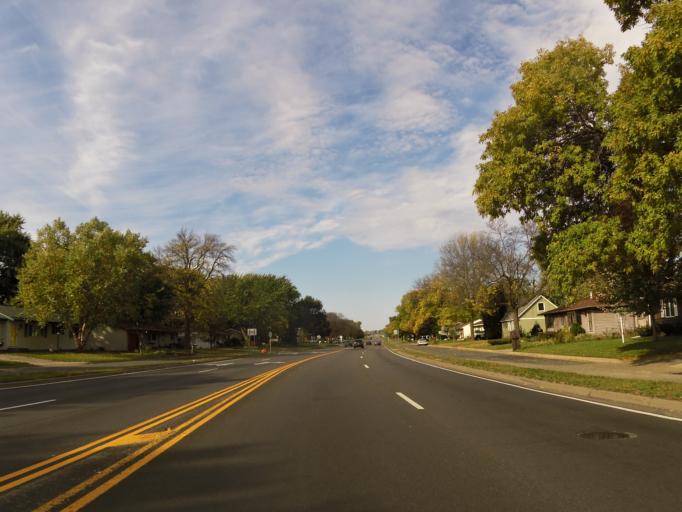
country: US
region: Minnesota
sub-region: Dakota County
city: Eagan
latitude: 44.8048
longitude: -93.2082
